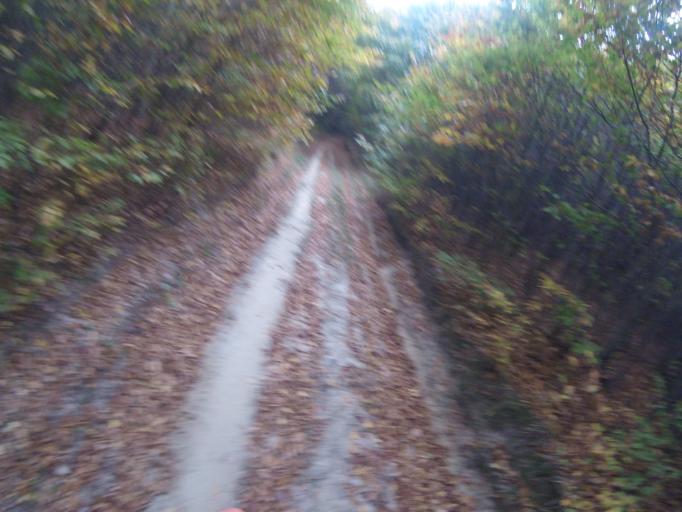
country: HU
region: Veszprem
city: Zirc
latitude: 47.2839
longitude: 17.7643
